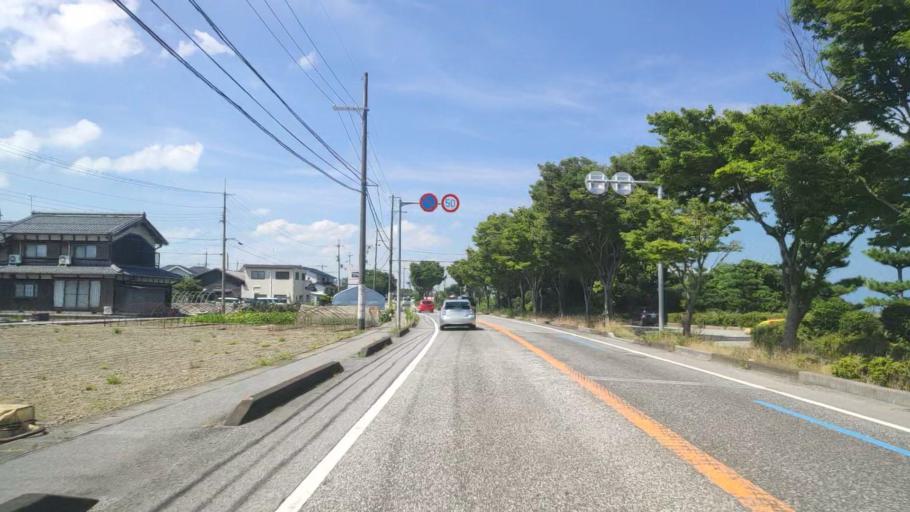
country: JP
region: Shiga Prefecture
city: Hikone
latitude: 35.2763
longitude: 136.2379
